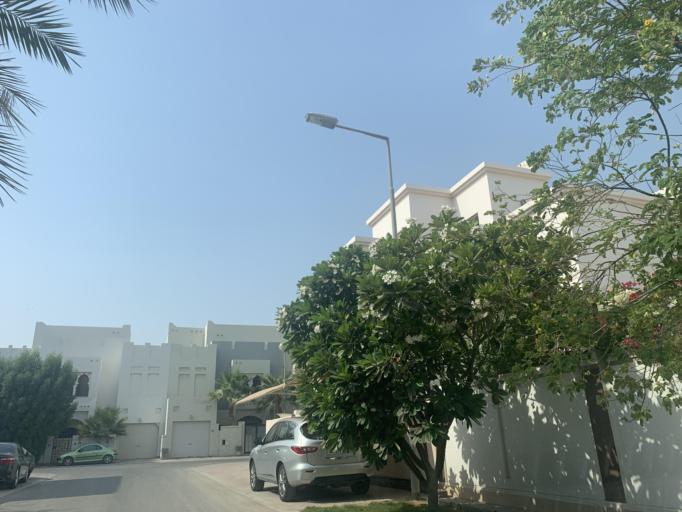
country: BH
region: Manama
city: Jidd Hafs
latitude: 26.2105
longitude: 50.4912
